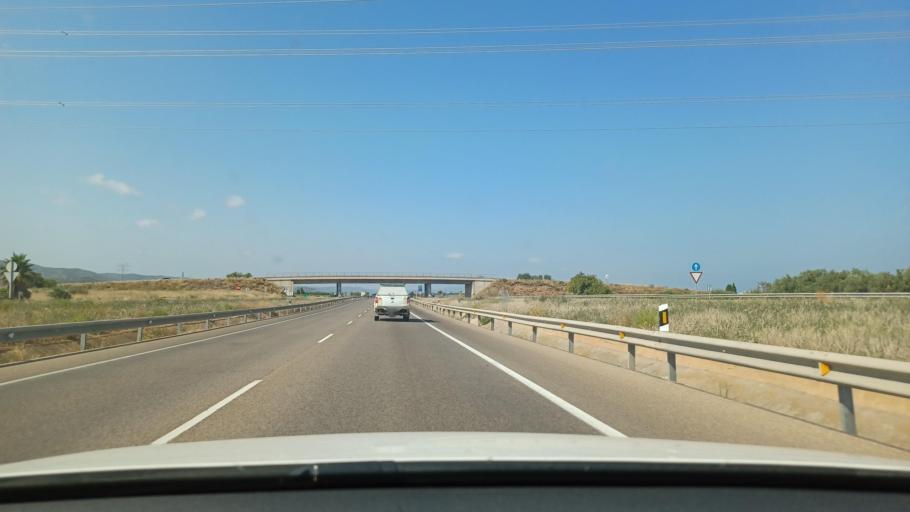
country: ES
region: Valencia
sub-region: Provincia de Castello
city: Orpesa/Oropesa del Mar
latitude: 40.1243
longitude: 0.1443
